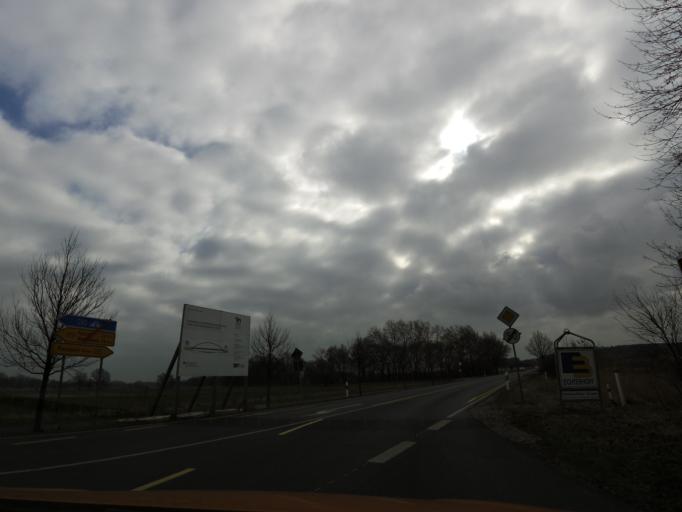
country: DE
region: Brandenburg
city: Werder
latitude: 52.4464
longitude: 12.9836
